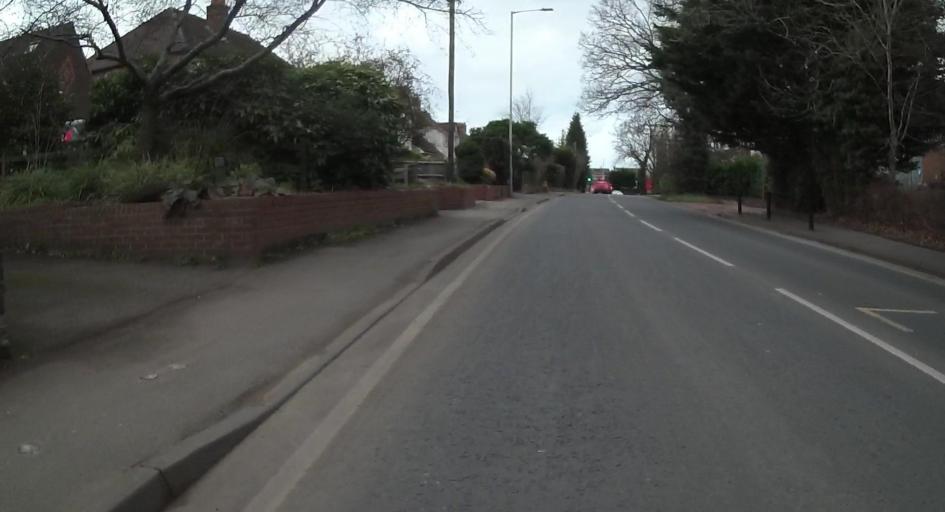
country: GB
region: England
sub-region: Wokingham
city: Wokingham
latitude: 51.4066
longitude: -0.8477
